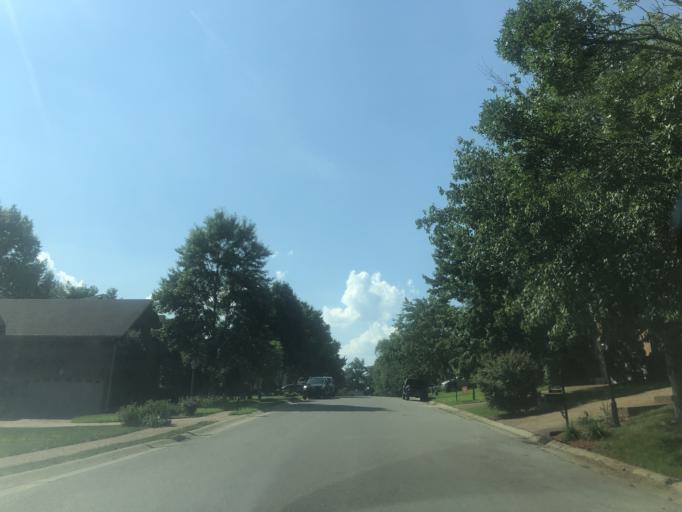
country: US
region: Tennessee
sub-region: Wilson County
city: Green Hill
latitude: 36.1508
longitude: -86.5913
